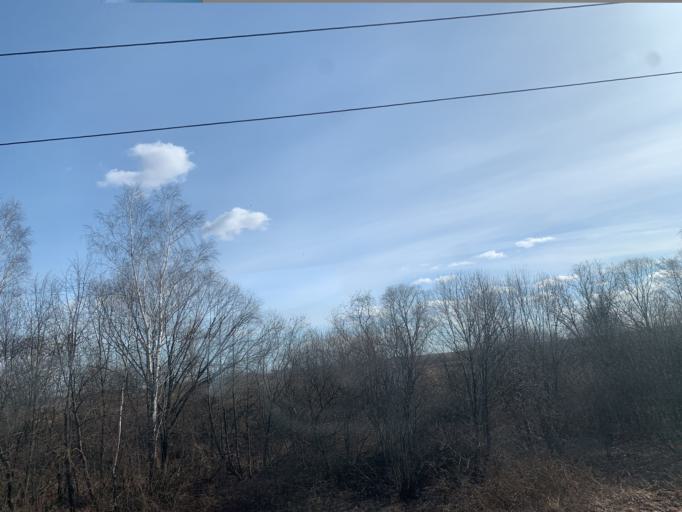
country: BY
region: Minsk
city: Stan'kava
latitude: 53.6841
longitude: 27.2162
